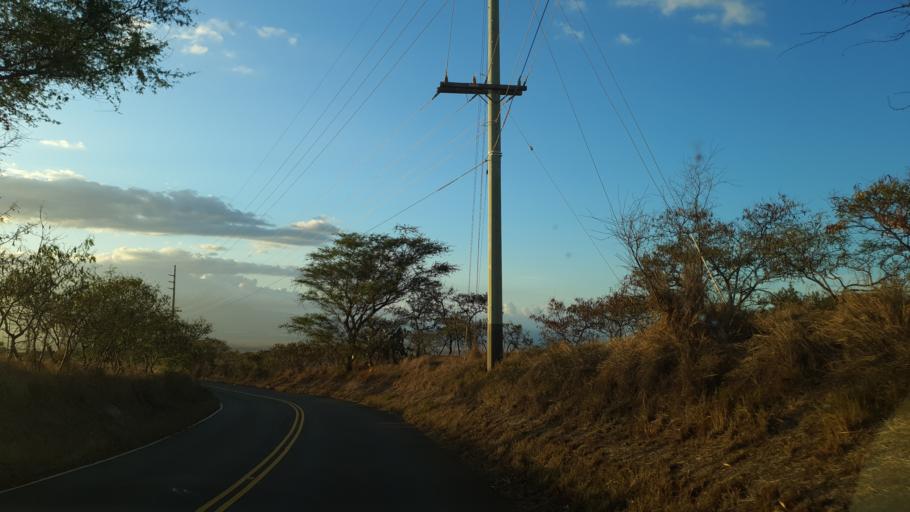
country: US
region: Hawaii
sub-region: Maui County
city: Pukalani
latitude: 20.7891
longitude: -156.3527
